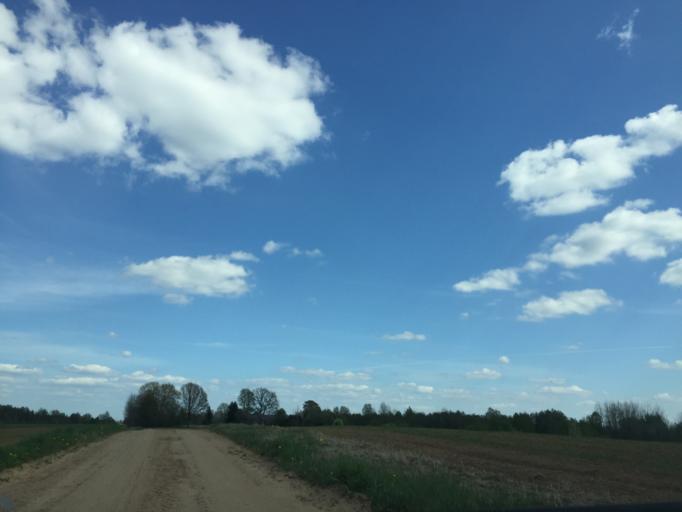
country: LV
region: Vecumnieki
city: Vecumnieki
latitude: 56.4787
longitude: 24.5754
